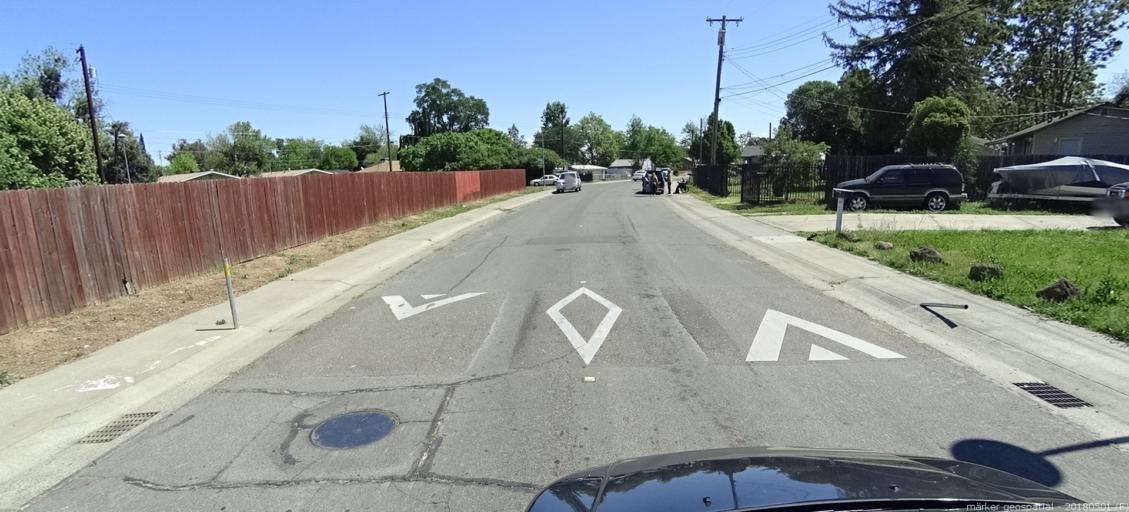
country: US
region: California
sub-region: Sacramento County
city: Rio Linda
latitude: 38.6306
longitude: -121.4435
